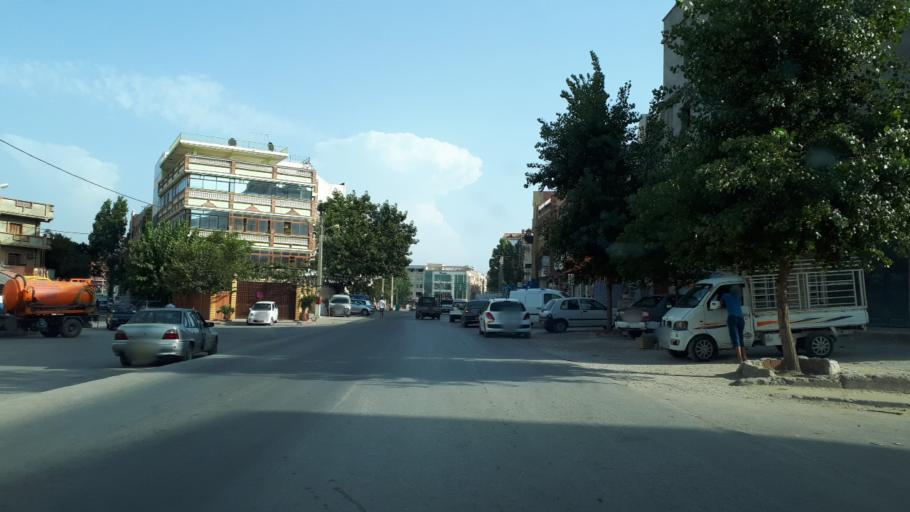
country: DZ
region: Alger
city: Dar el Beida
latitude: 36.7328
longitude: 3.2352
